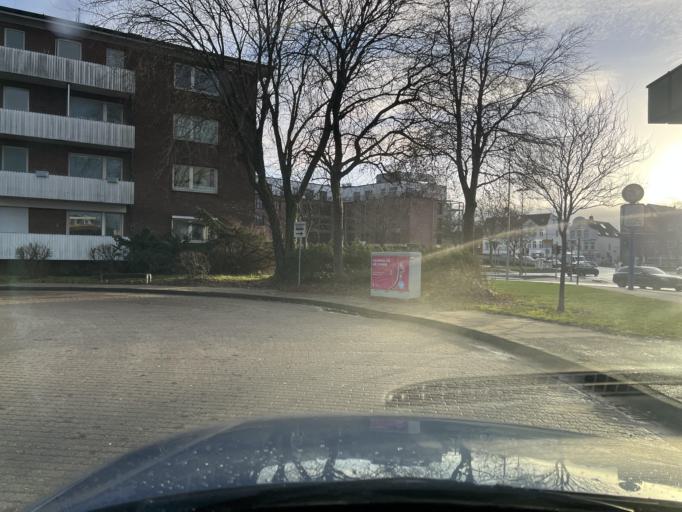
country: DE
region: Schleswig-Holstein
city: Heide
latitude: 54.1959
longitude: 9.0972
